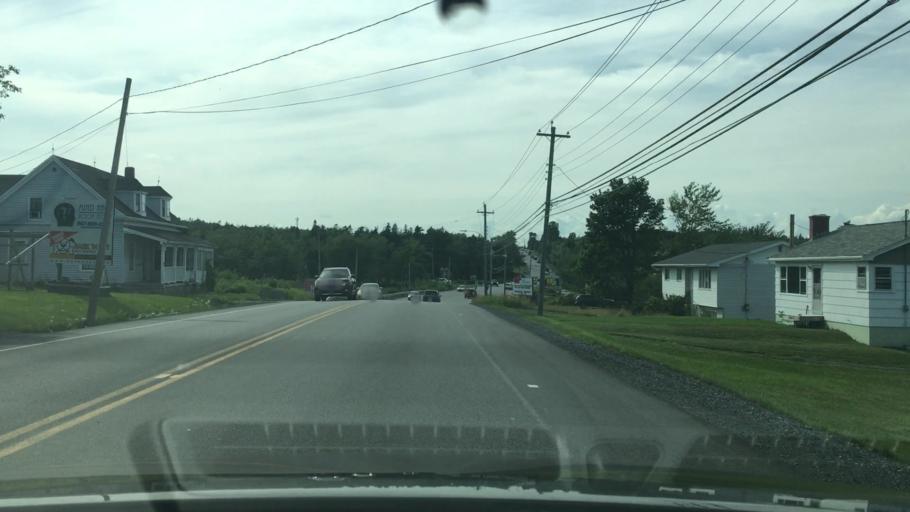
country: CA
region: Nova Scotia
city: Dartmouth
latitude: 44.7280
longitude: -63.7475
